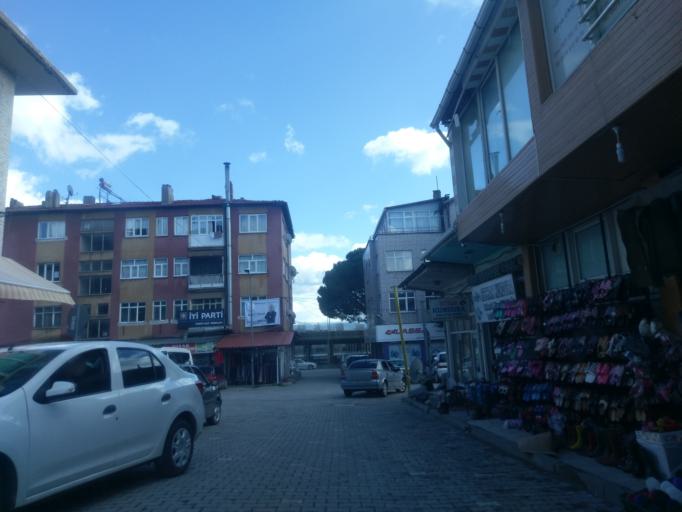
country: TR
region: Kuetahya
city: Gediz
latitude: 38.9886
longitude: 29.3969
